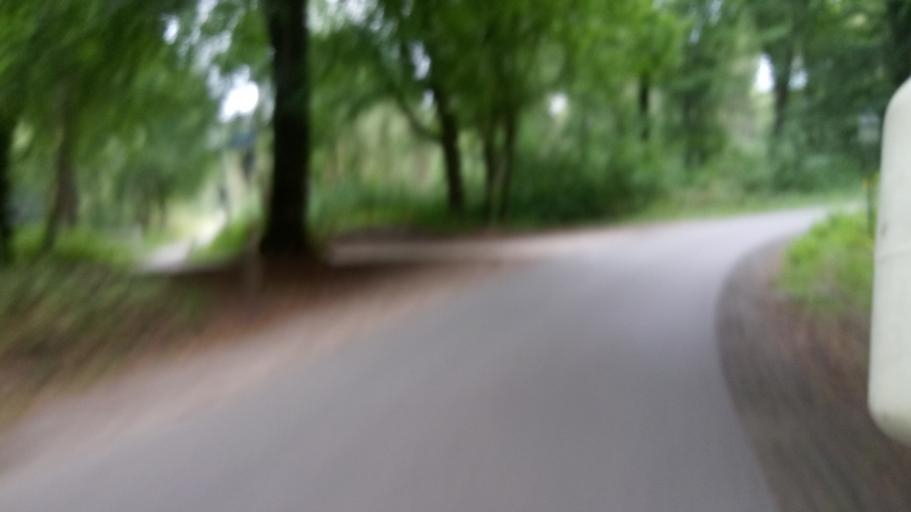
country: NL
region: Gelderland
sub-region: Gemeente Voorst
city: Voorst
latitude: 52.1781
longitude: 6.1134
